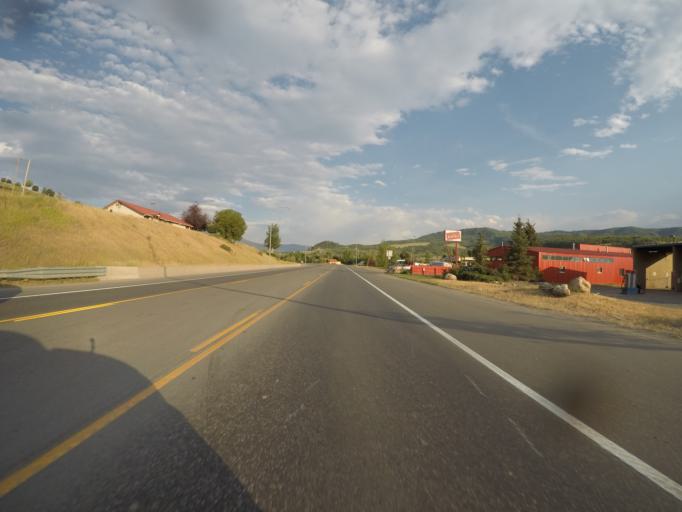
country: US
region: Colorado
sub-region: Routt County
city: Steamboat Springs
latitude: 40.4968
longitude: -106.8534
